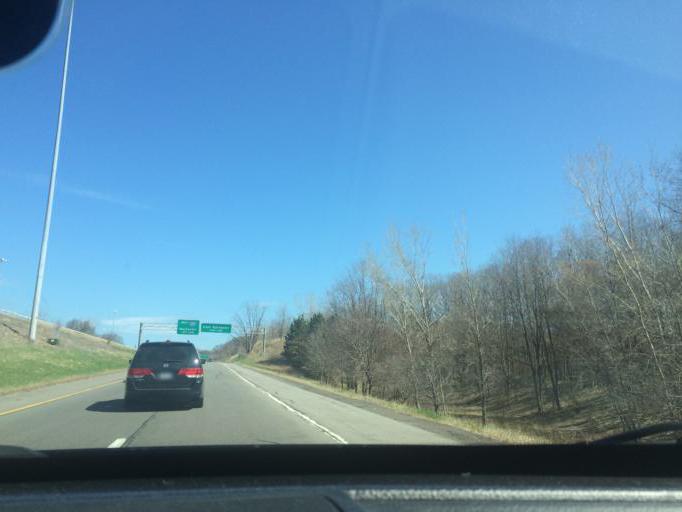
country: US
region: New York
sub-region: Monroe County
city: East Rochester
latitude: 43.1110
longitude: -77.5063
